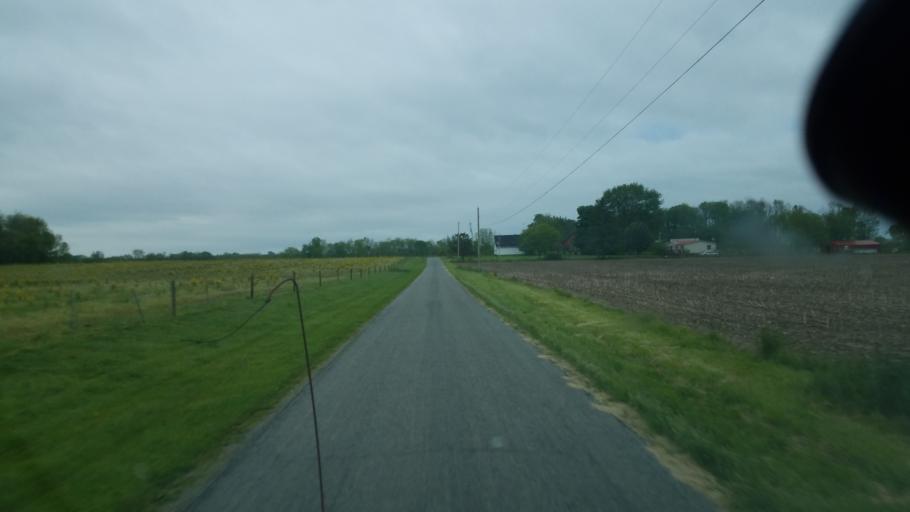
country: US
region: Ohio
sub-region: Highland County
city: Greenfield
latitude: 39.3348
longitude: -83.4348
